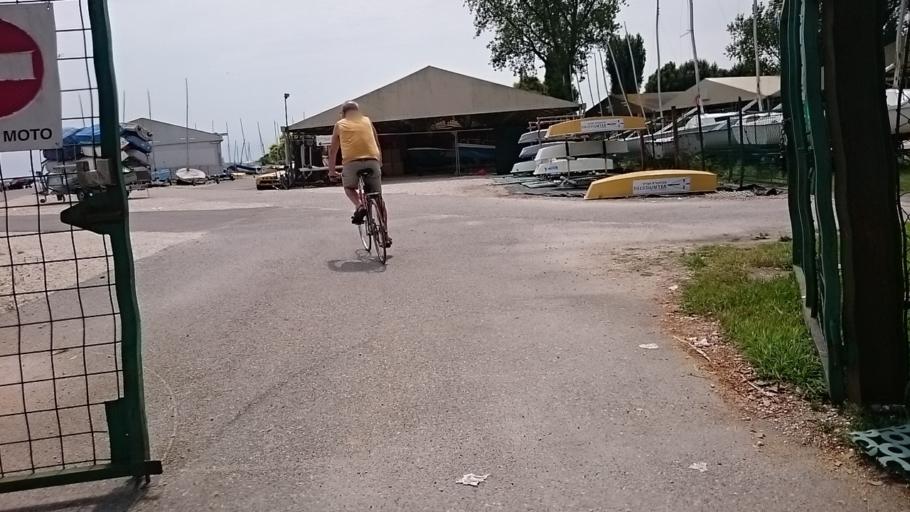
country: IT
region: Veneto
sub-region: Provincia di Venezia
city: Campalto
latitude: 45.4671
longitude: 12.2817
